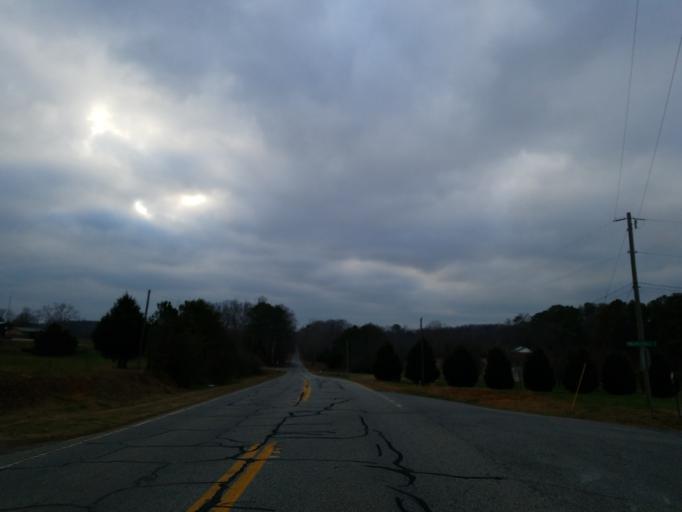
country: US
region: Georgia
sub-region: Bartow County
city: Rydal
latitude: 34.3465
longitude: -84.6977
